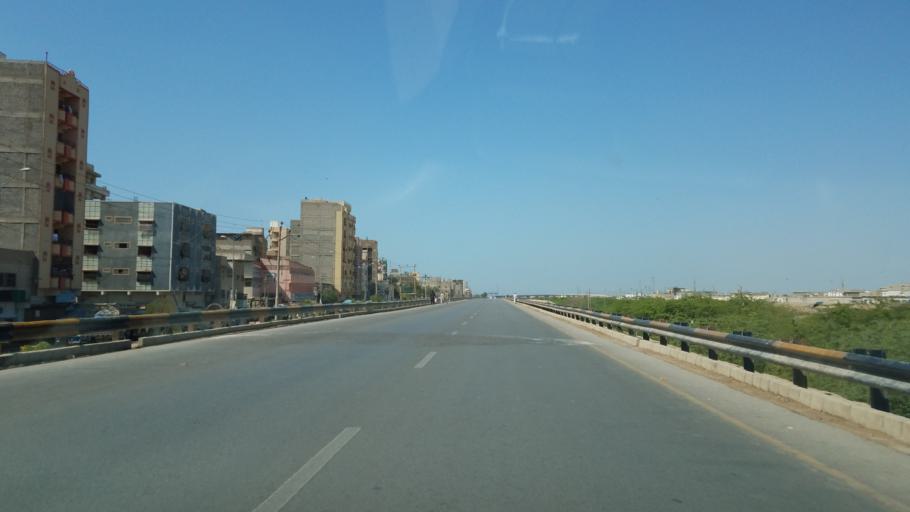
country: PK
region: Sindh
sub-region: Karachi District
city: Karachi
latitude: 24.8765
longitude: 66.9877
